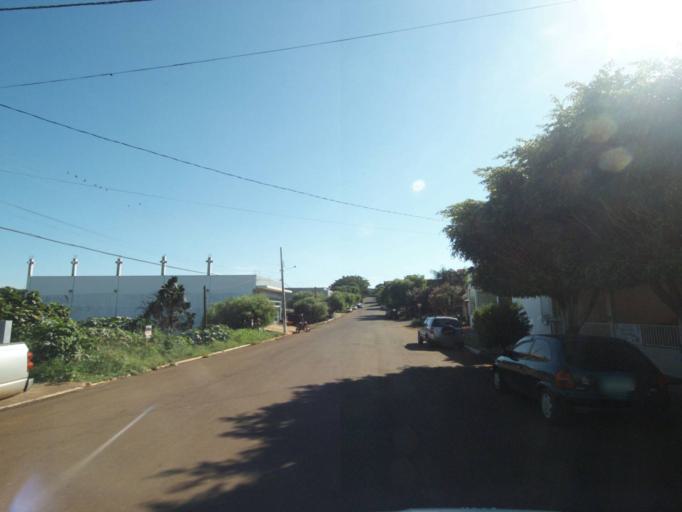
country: BR
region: Parana
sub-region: Laranjeiras Do Sul
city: Laranjeiras do Sul
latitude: -25.4906
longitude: -52.5286
